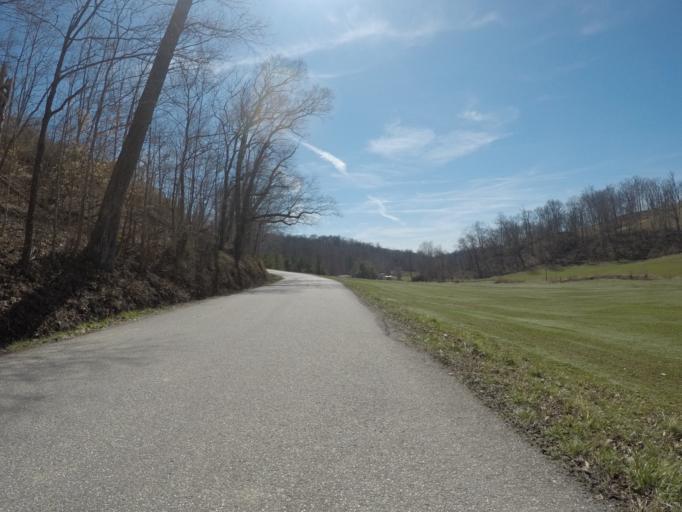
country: US
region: Ohio
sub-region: Lawrence County
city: South Point
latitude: 38.4758
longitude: -82.5658
